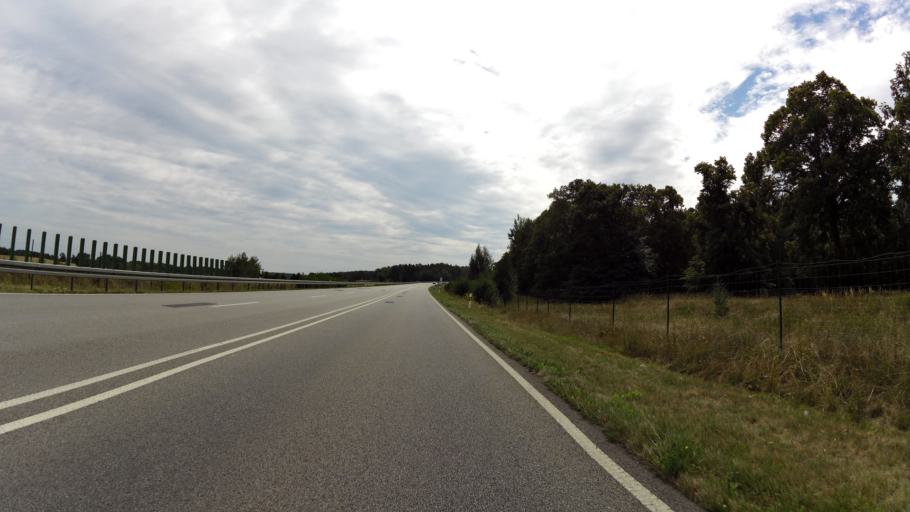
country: DE
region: Brandenburg
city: Neuzelle
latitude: 52.0454
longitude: 14.6743
